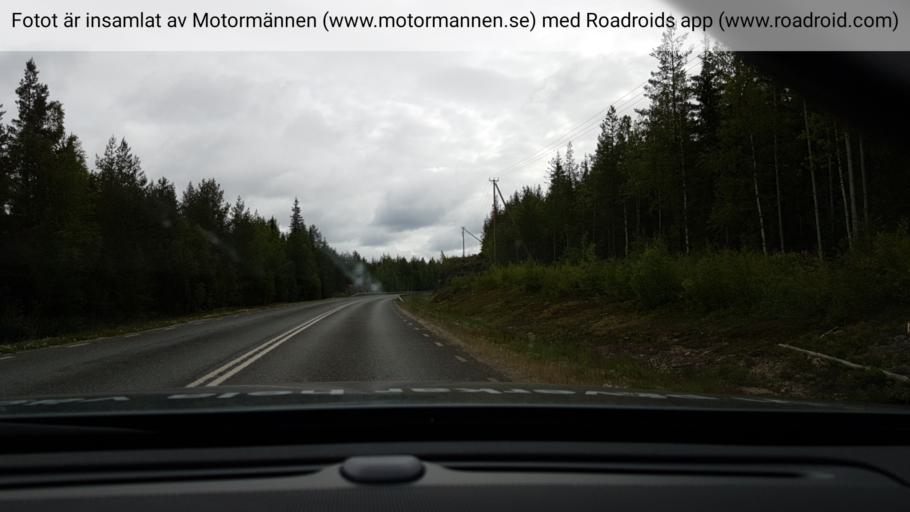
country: SE
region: Vaesterbotten
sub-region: Lycksele Kommun
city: Lycksele
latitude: 64.5721
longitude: 18.6237
